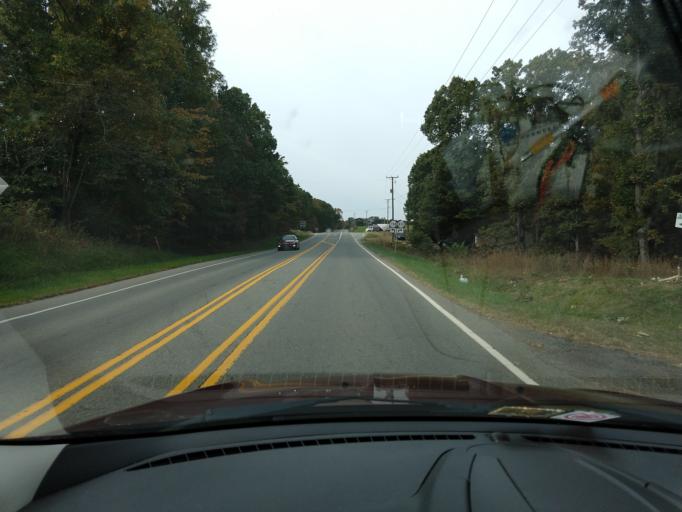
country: US
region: Virginia
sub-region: Franklin County
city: Union Hall
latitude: 36.9933
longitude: -79.7117
